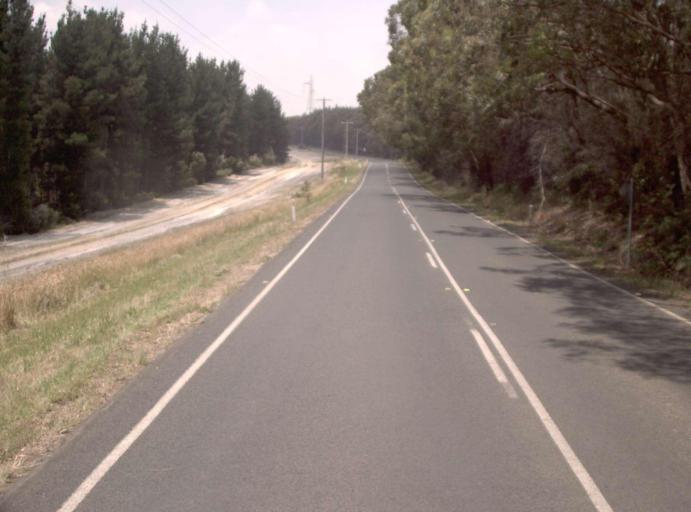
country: AU
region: Victoria
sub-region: Latrobe
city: Traralgon
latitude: -38.2586
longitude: 146.6785
